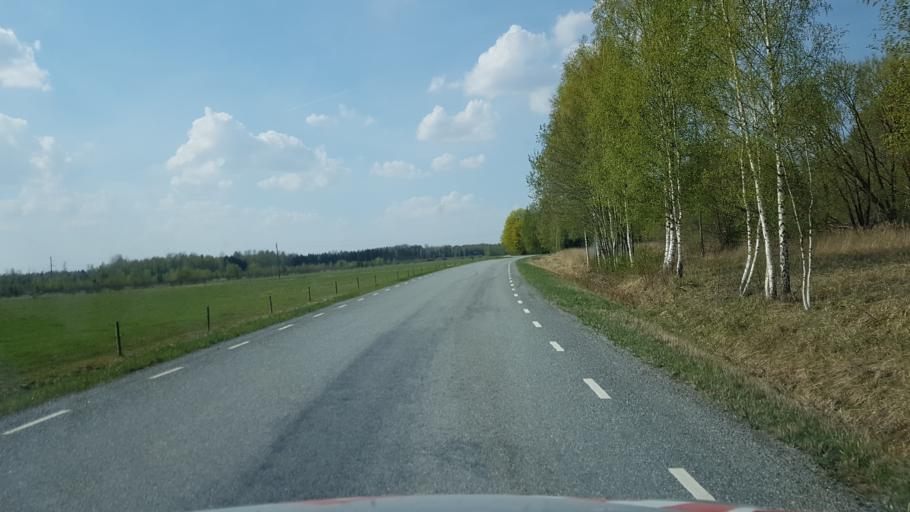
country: EE
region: Paernumaa
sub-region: Sindi linn
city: Sindi
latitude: 58.4339
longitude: 24.6244
